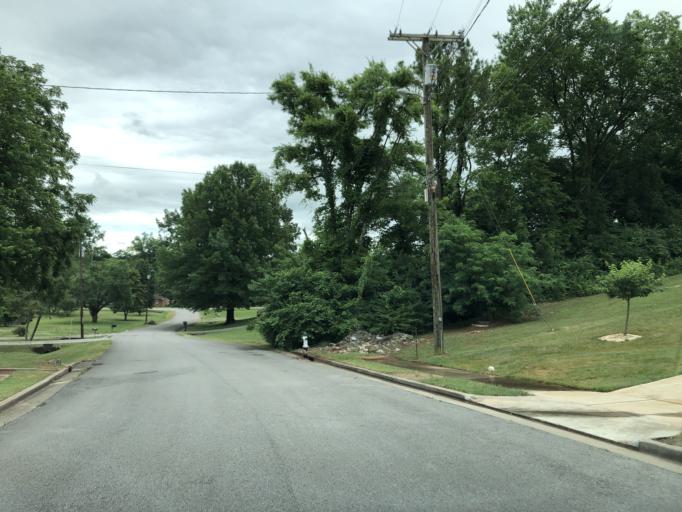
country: US
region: Tennessee
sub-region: Davidson County
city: Goodlettsville
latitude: 36.2736
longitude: -86.7678
